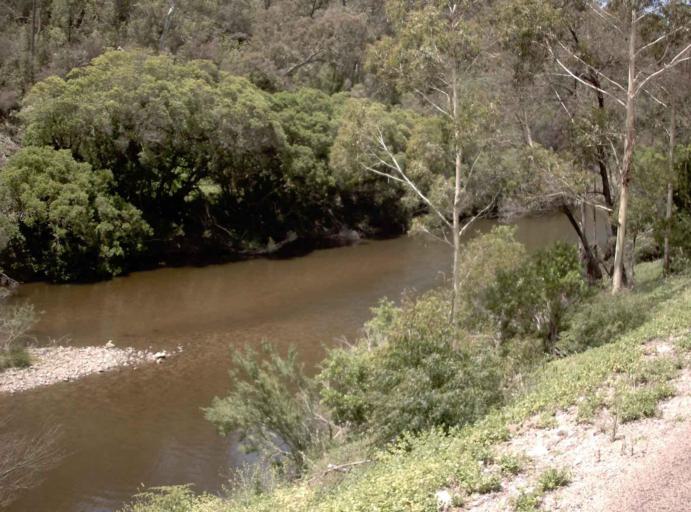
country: AU
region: Victoria
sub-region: East Gippsland
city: Lakes Entrance
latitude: -37.5430
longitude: 147.8656
